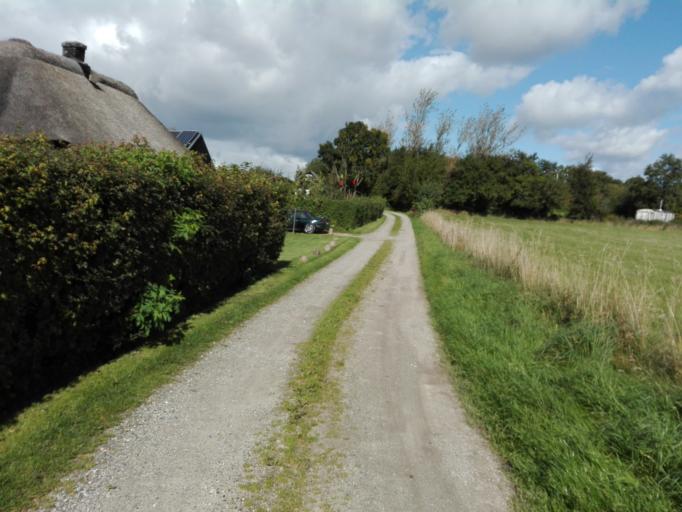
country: DK
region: Central Jutland
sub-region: Arhus Kommune
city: Beder
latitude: 56.0581
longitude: 10.2228
